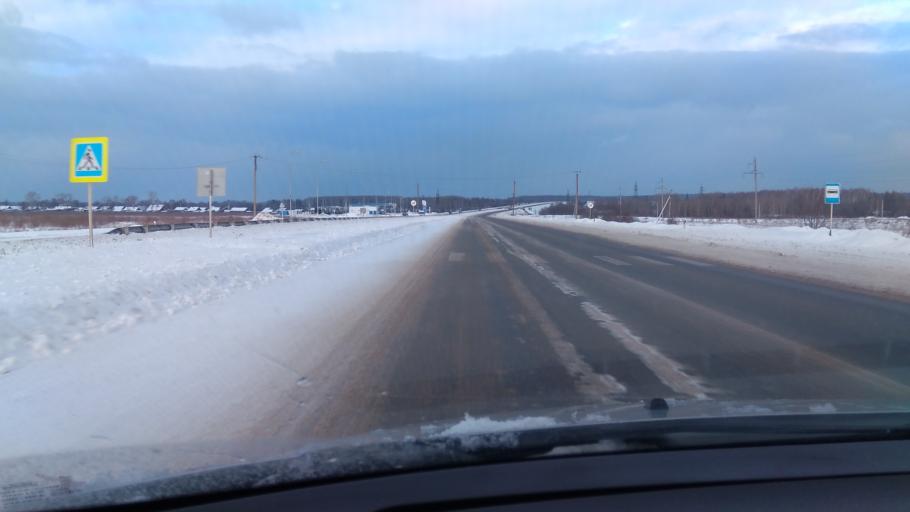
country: RU
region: Sverdlovsk
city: Tsementnyy
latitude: 57.4939
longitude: 60.1764
